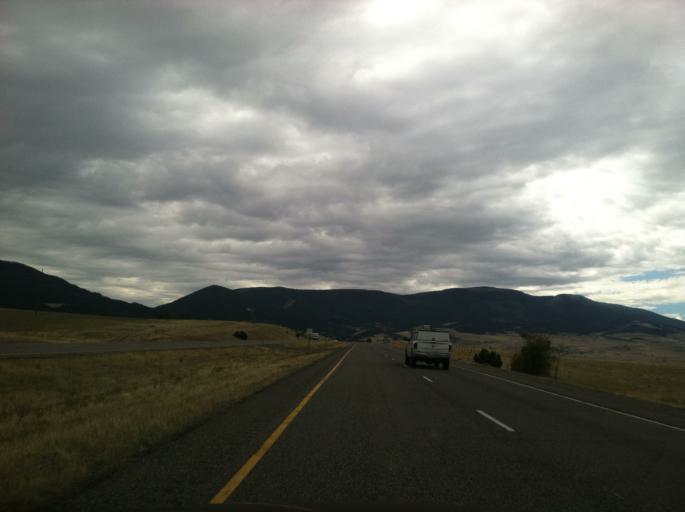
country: US
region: Montana
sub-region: Park County
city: Livingston
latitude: 45.6523
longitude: -110.5422
